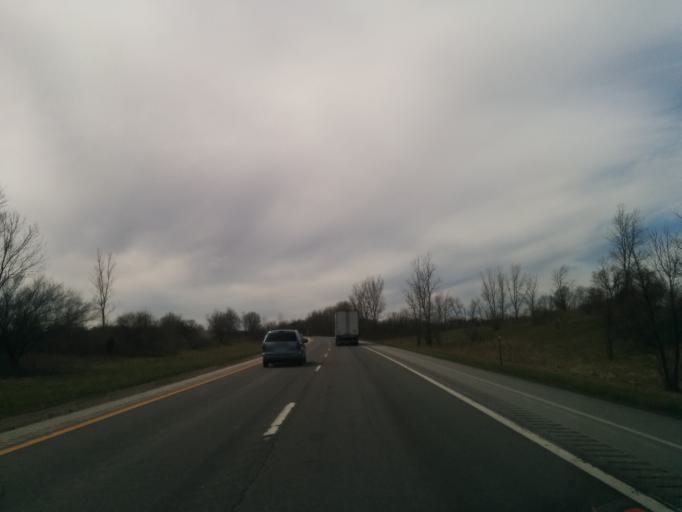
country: US
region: Michigan
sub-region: Ottawa County
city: Zeeland
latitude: 42.7616
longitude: -86.0491
